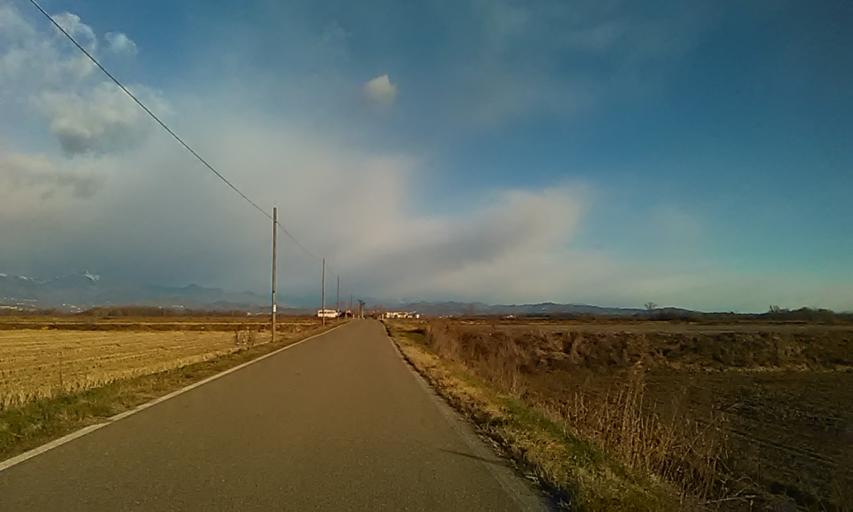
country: IT
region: Piedmont
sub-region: Provincia di Vercelli
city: Buronzo
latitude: 45.4976
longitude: 8.2698
